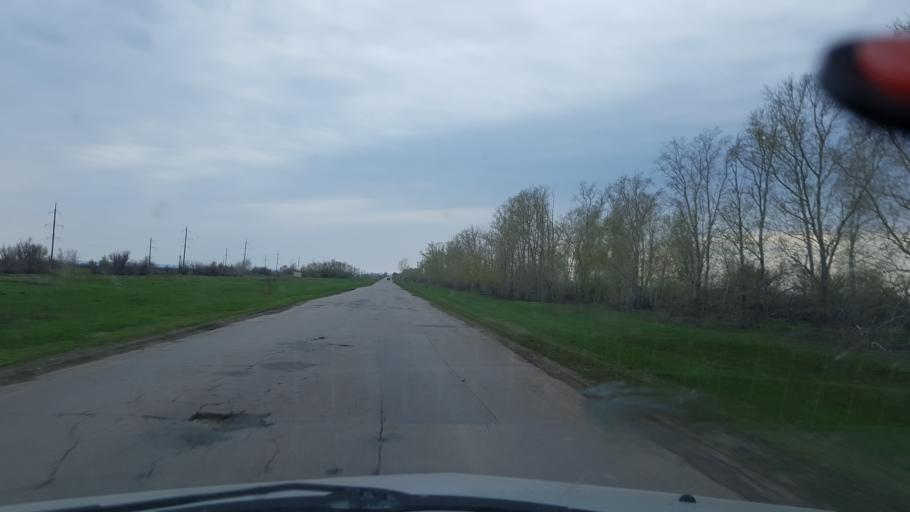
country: RU
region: Samara
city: Khryashchevka
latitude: 53.6681
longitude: 49.1427
